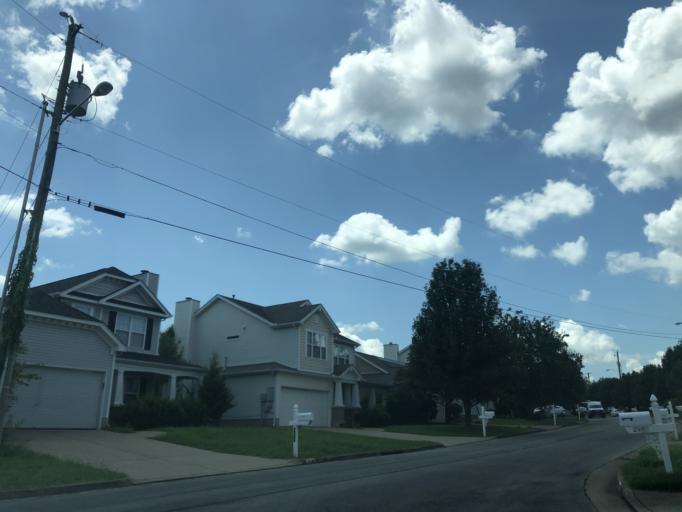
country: US
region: Tennessee
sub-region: Wilson County
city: Green Hill
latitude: 36.2214
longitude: -86.5918
